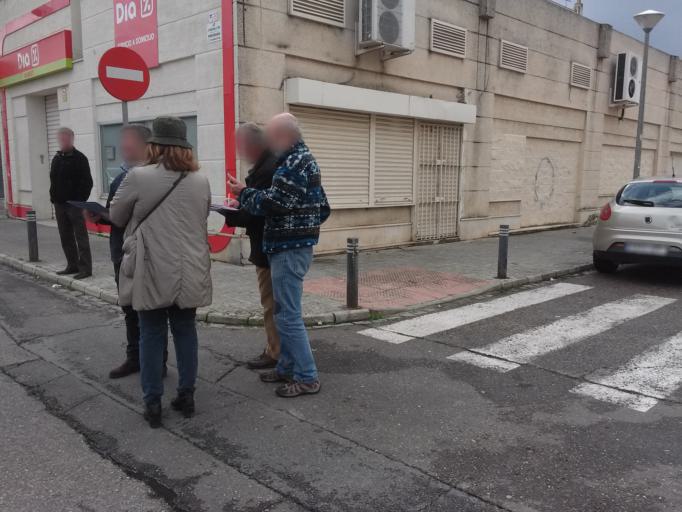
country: ES
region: Andalusia
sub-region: Provincia de Sevilla
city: La Algaba
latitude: 37.4268
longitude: -5.9856
